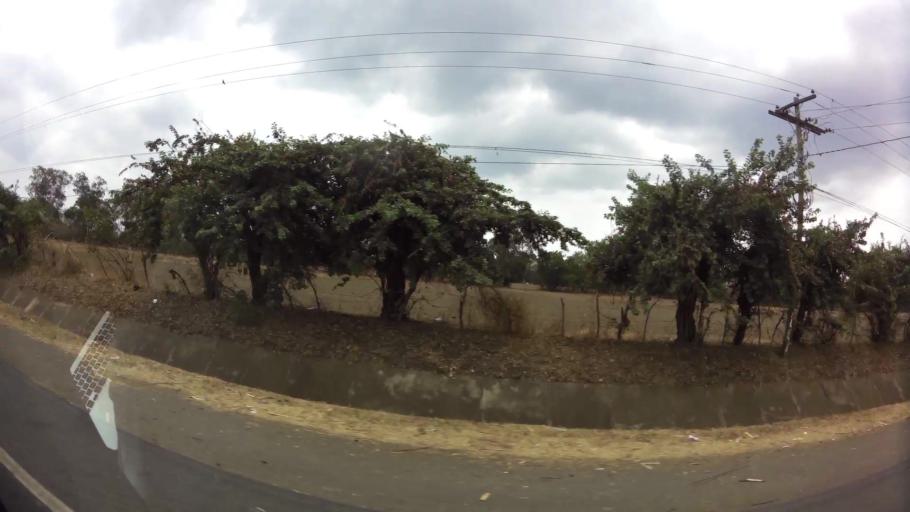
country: NI
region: Leon
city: Telica
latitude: 12.4843
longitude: -86.8616
